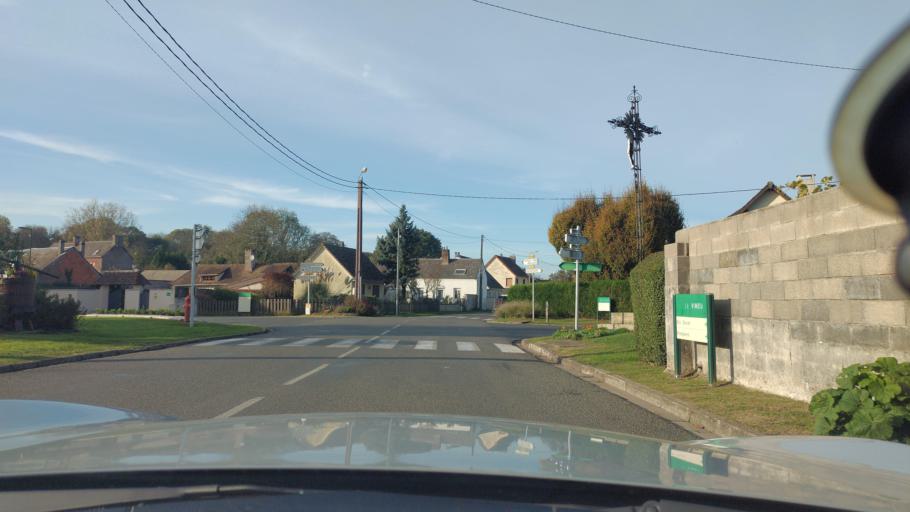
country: FR
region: Picardie
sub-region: Departement de la Somme
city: Friville-Escarbotin
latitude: 50.1060
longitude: 1.5282
